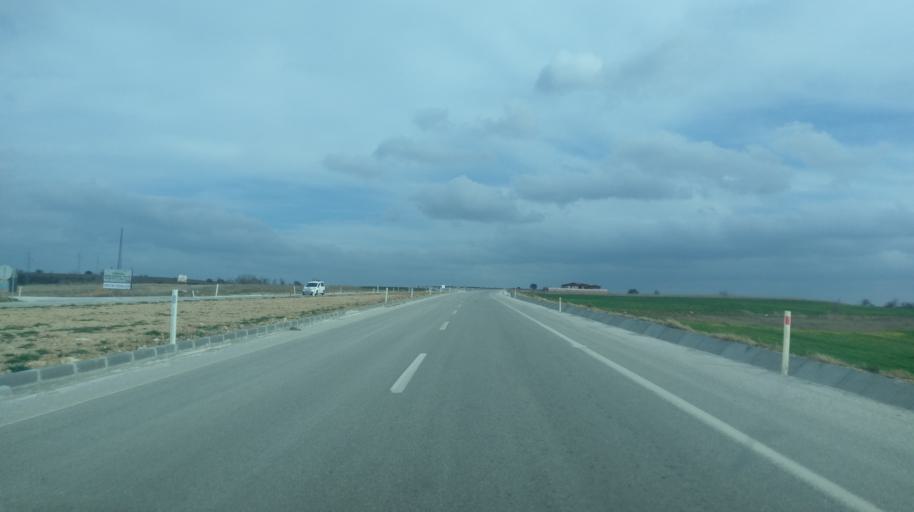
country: TR
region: Kirklareli
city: Inece
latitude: 41.6805
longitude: 27.0972
